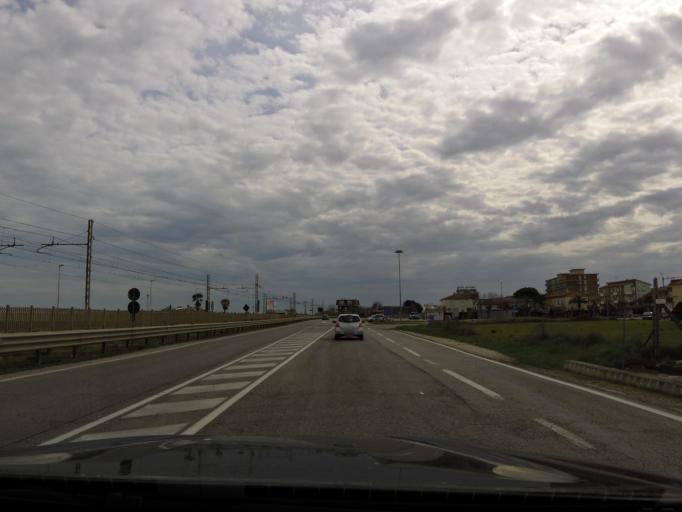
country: IT
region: The Marches
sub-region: Provincia di Macerata
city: Porto Recanati
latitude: 43.4091
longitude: 13.6762
